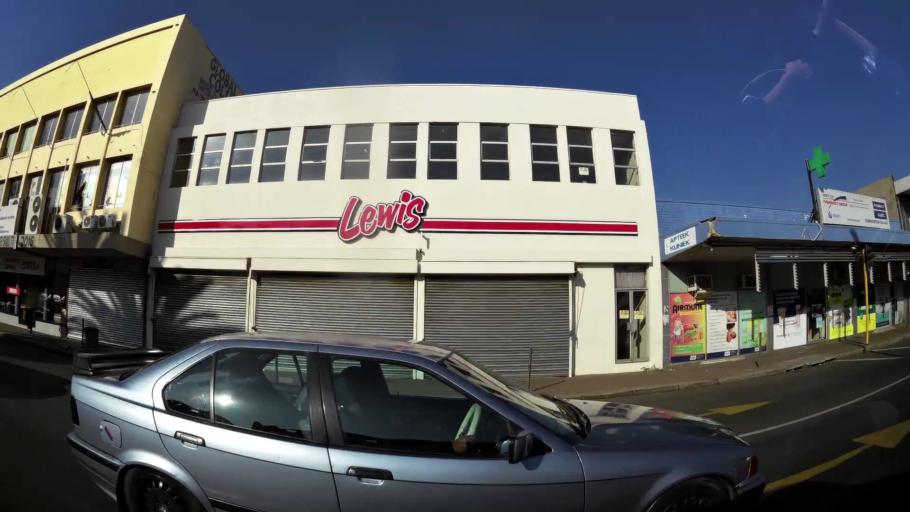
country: ZA
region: Gauteng
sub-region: West Rand District Municipality
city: Randfontein
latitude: -26.1788
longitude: 27.7043
